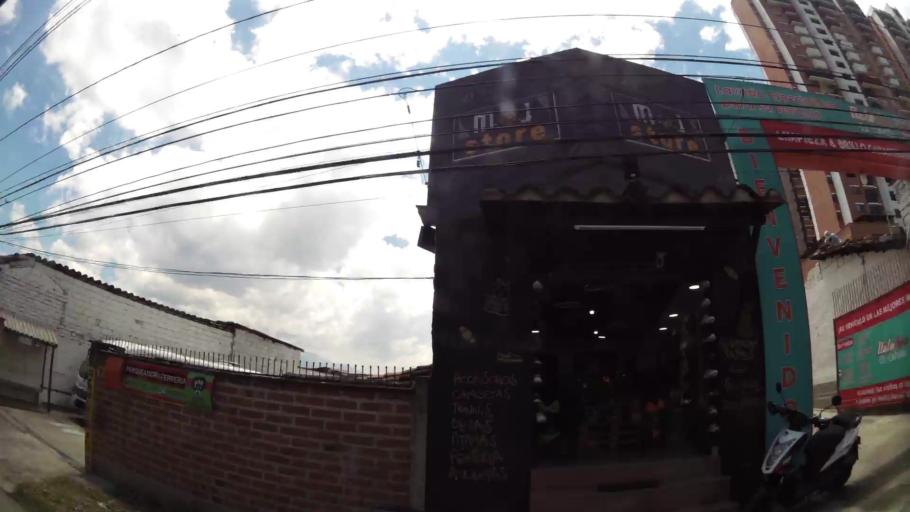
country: CO
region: Antioquia
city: La Estrella
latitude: 6.1655
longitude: -75.6453
